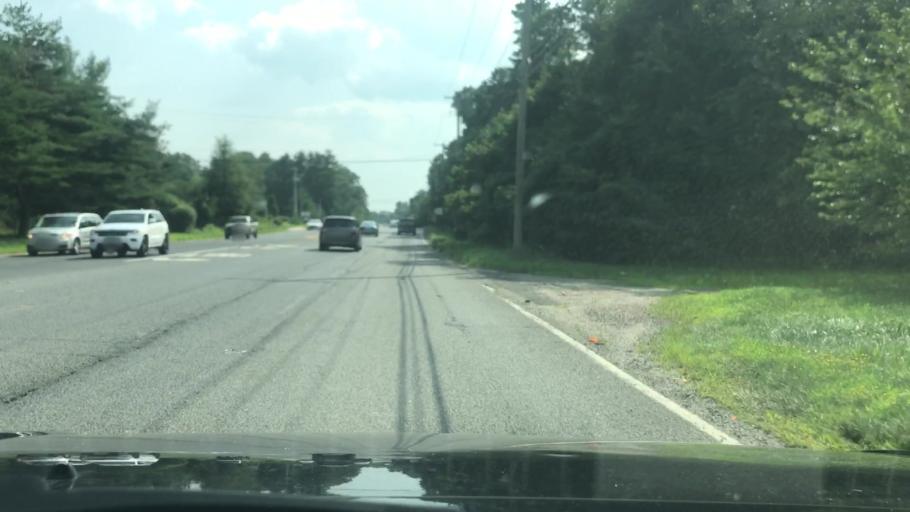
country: US
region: New Jersey
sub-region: Monmouth County
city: Farmingdale
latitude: 40.2315
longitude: -74.1125
